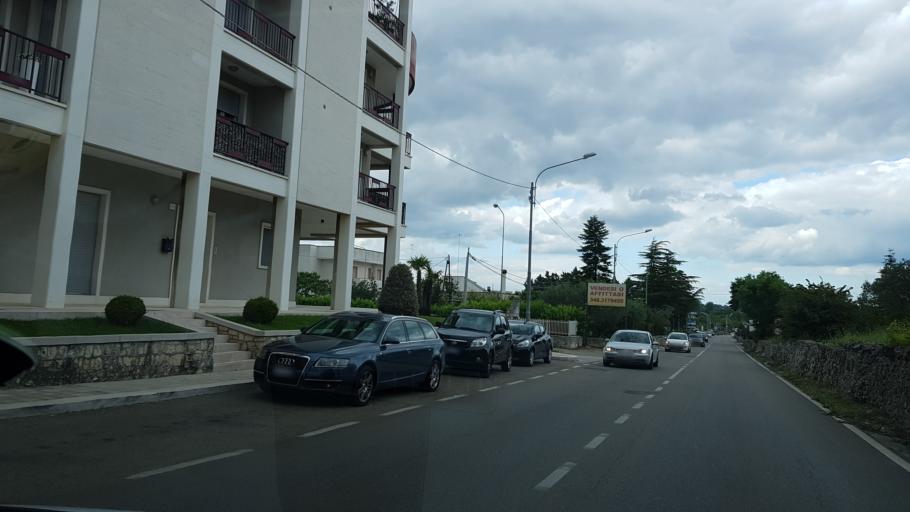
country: IT
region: Apulia
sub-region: Provincia di Bari
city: Locorotondo
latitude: 40.7612
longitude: 17.3297
